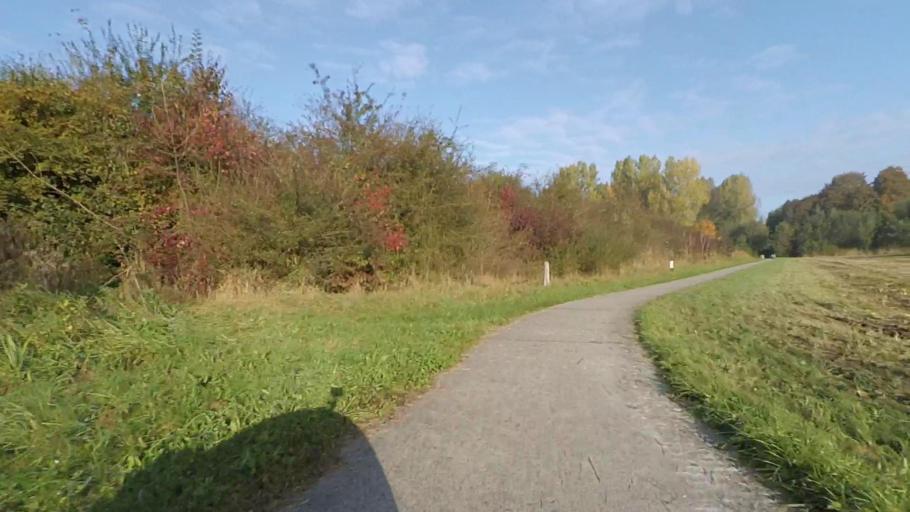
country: NL
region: Flevoland
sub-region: Gemeente Zeewolde
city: Zeewolde
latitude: 52.2891
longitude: 5.5289
